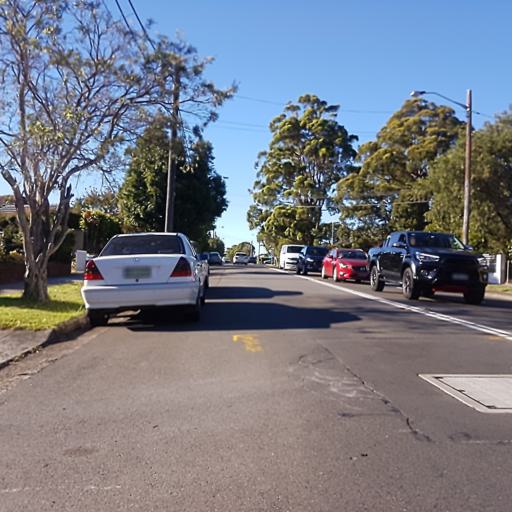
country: AU
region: New South Wales
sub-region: Willoughby
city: Castle Cove
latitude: -33.8039
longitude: 151.2041
